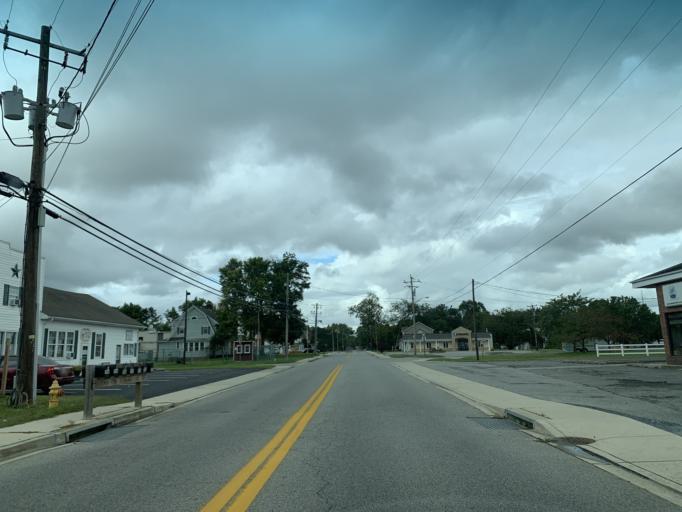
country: US
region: Maryland
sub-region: Caroline County
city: Denton
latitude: 38.8789
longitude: -75.8280
